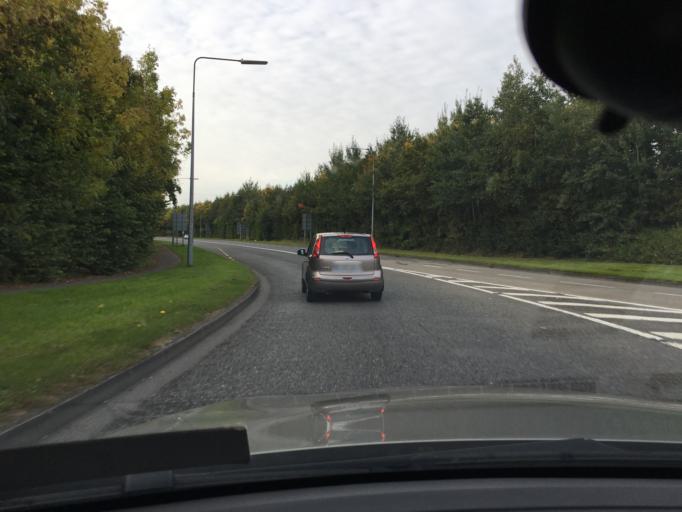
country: IE
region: Leinster
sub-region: An Longfort
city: Longford
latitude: 53.7386
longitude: -7.7783
